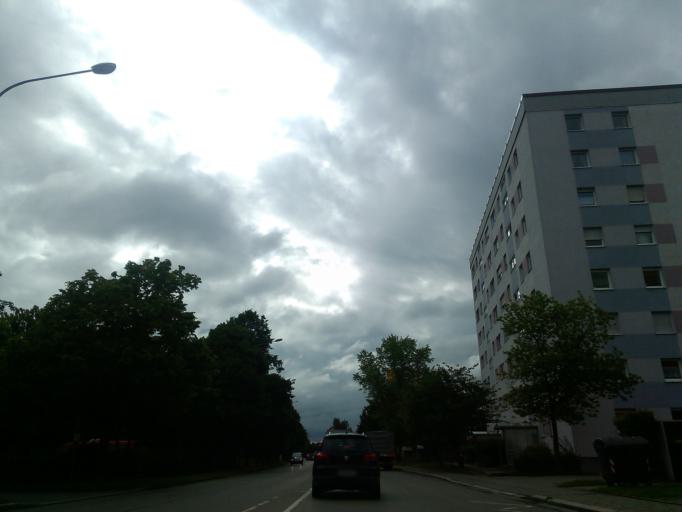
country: DE
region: Bavaria
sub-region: Swabia
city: Konigsbrunn
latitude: 48.2814
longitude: 10.8887
